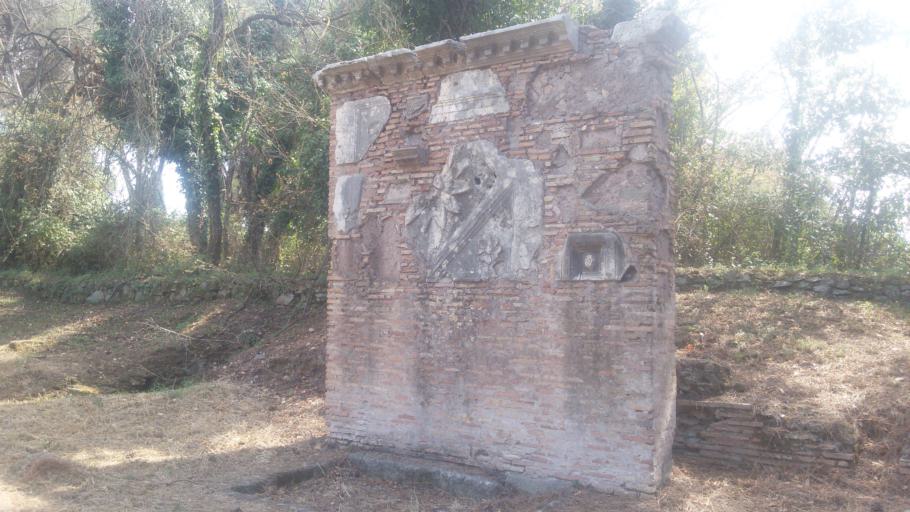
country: IT
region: Latium
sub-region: Citta metropolitana di Roma Capitale
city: Rome
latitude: 41.8371
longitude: 12.5375
